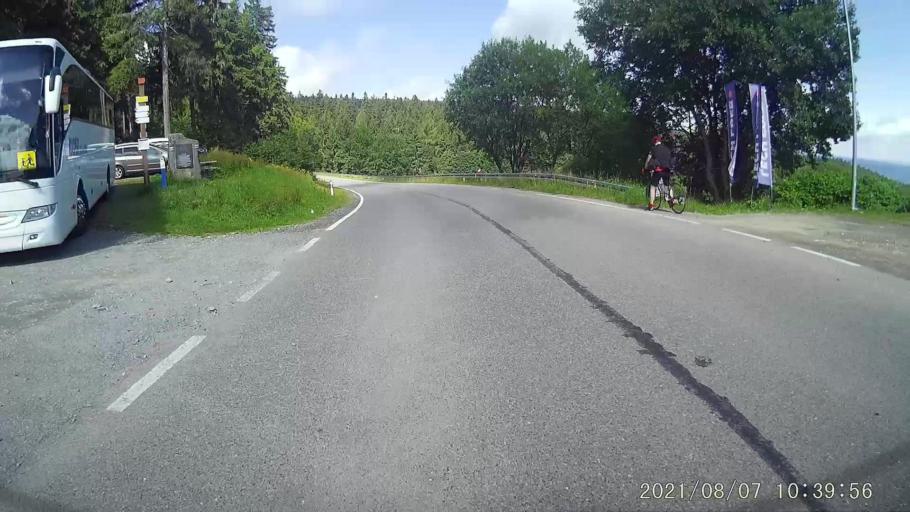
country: PL
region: Lower Silesian Voivodeship
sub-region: Powiat klodzki
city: Duszniki-Zdroj
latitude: 50.3474
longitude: 16.3813
